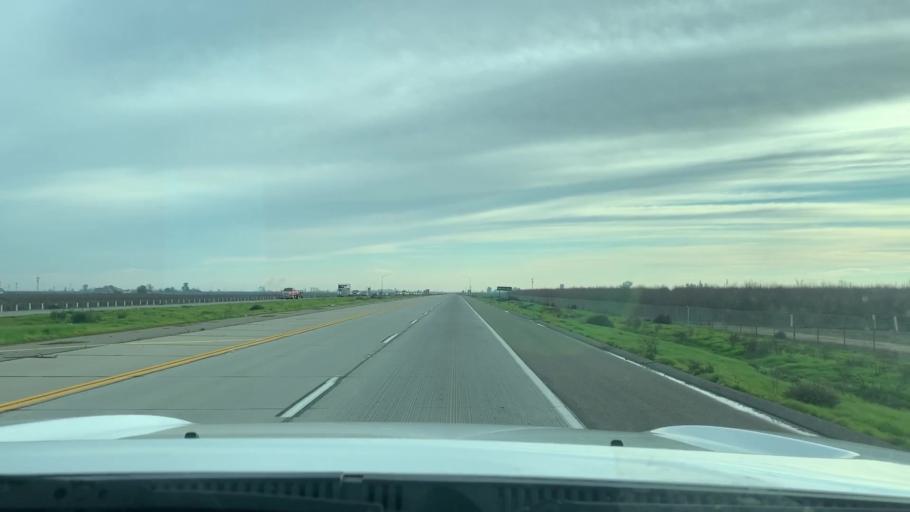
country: US
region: California
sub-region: Fresno County
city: Caruthers
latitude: 36.5804
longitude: -119.7862
